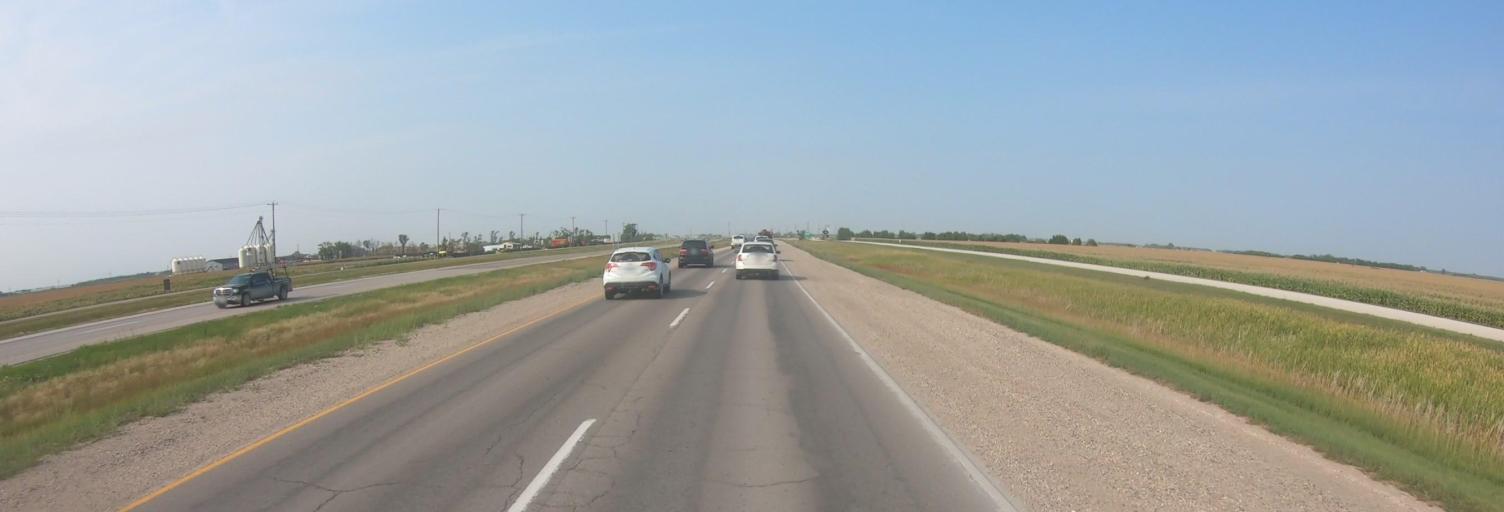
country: CA
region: Manitoba
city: Steinbach
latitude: 49.5692
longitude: -96.6875
